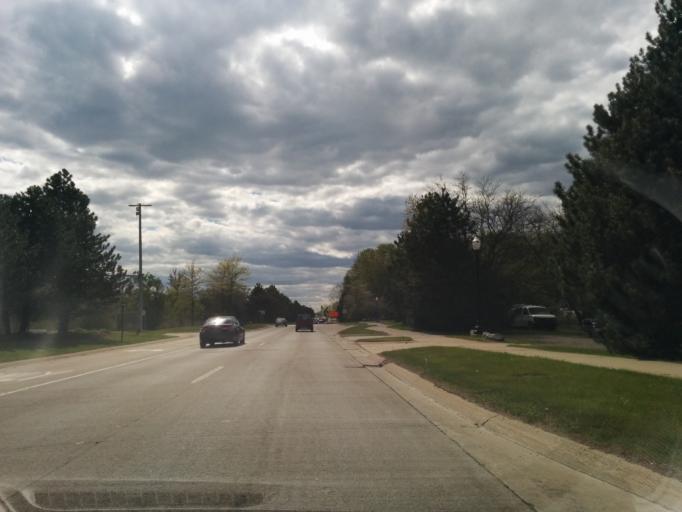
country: US
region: Michigan
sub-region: Oakland County
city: Farmington Hills
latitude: 42.4979
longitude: -83.4096
